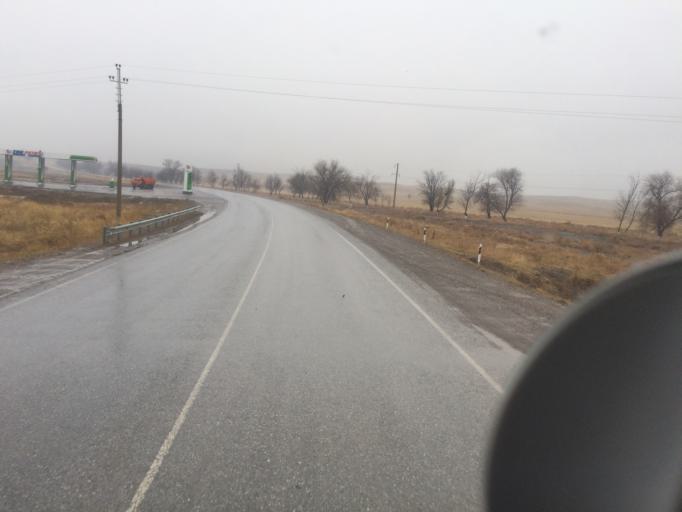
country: KG
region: Chuy
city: Kant
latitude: 43.0045
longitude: 74.8616
